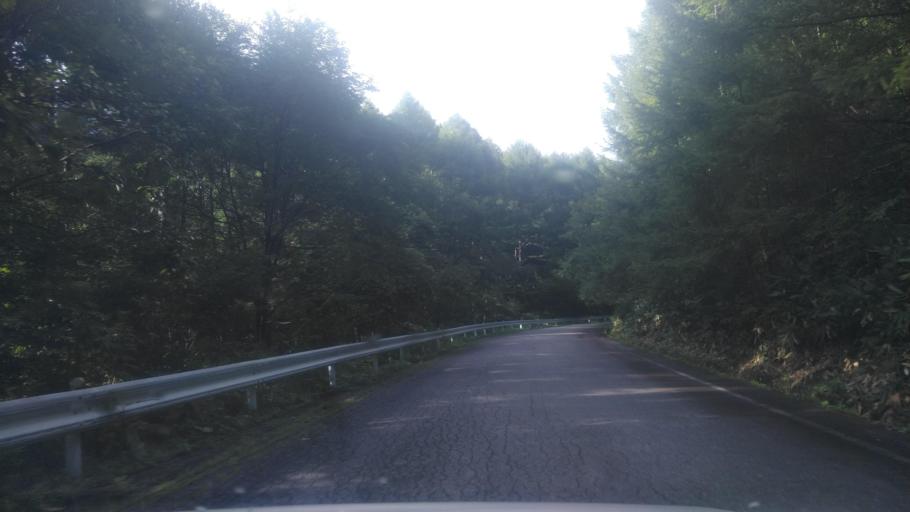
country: JP
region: Nagano
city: Ueda
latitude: 36.5087
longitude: 138.3749
